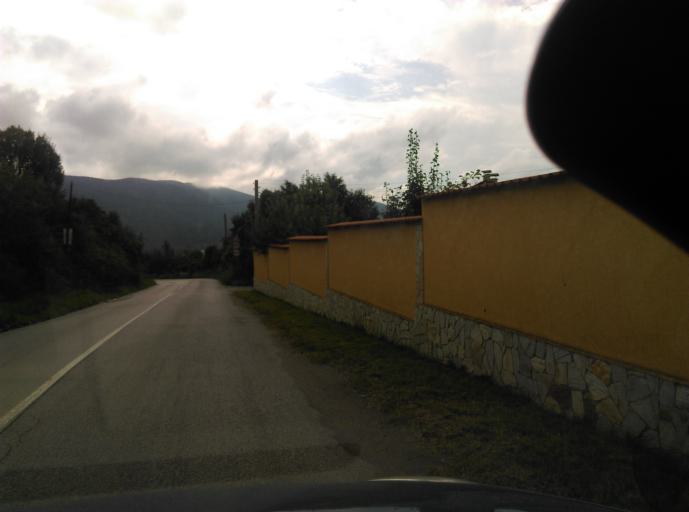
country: BG
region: Sofia-Capital
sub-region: Stolichna Obshtina
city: Sofia
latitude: 42.5891
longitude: 23.4021
